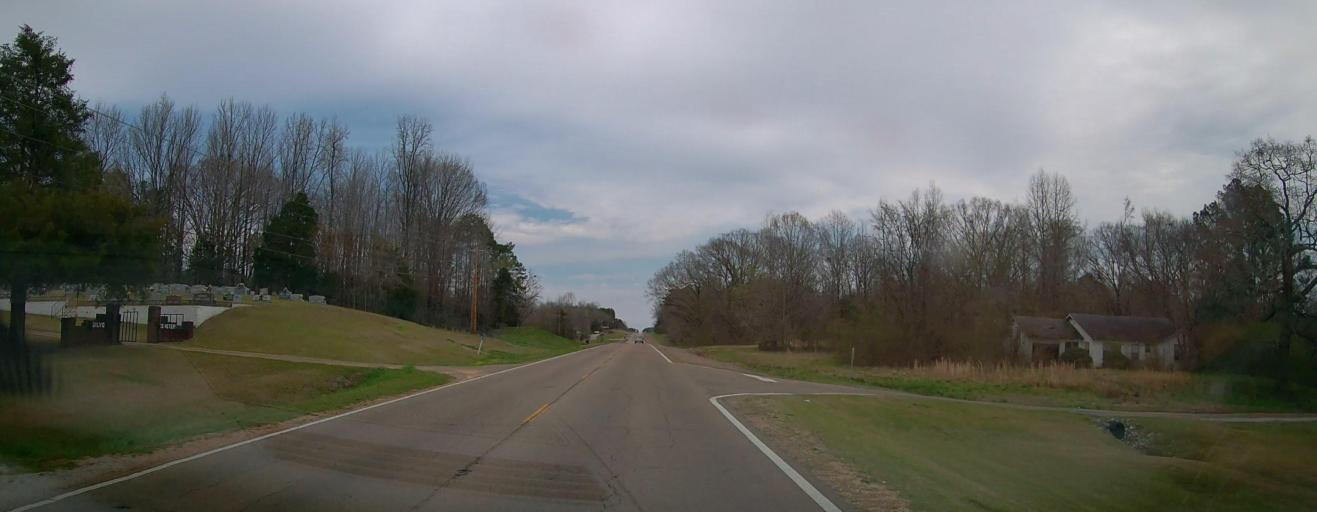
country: US
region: Mississippi
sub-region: Lee County
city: Plantersville
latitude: 34.2659
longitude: -88.6206
